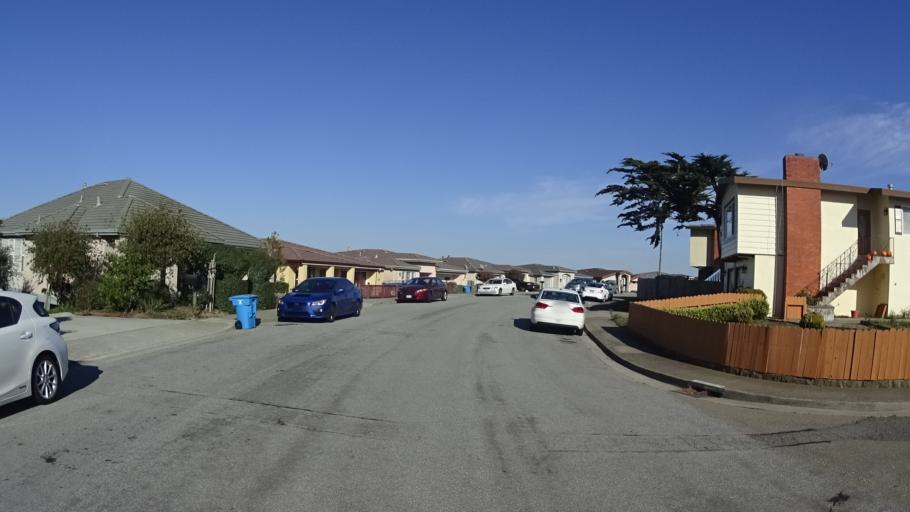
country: US
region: California
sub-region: San Mateo County
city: Pacifica
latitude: 37.6318
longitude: -122.4580
